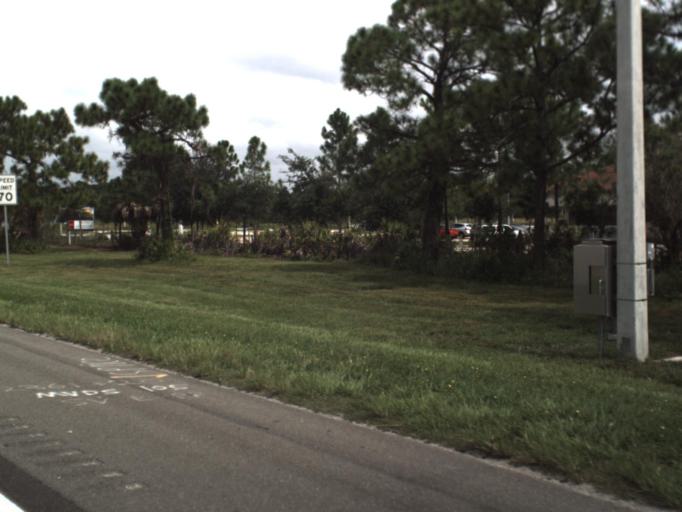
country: US
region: Florida
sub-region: Sarasota County
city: The Meadows
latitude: 27.3997
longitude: -82.4516
